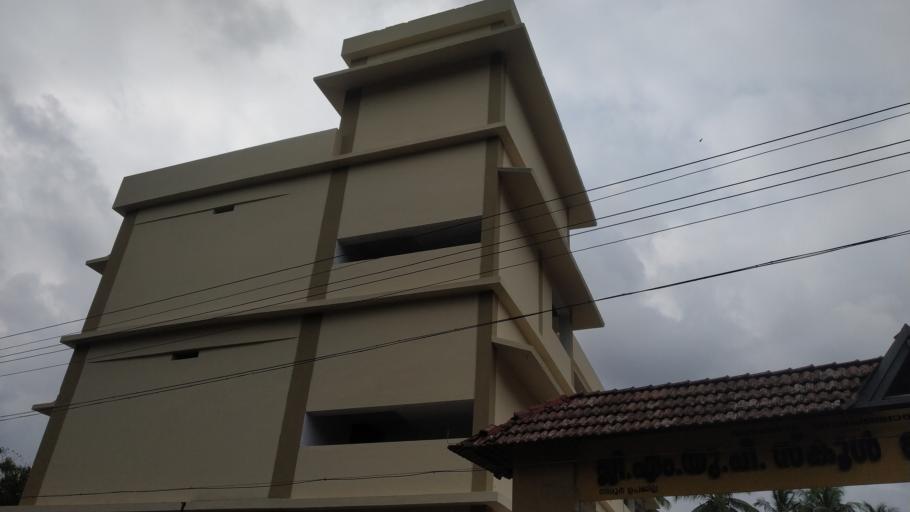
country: IN
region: Kerala
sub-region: Malappuram
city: Tirur
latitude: 10.8843
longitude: 75.9331
